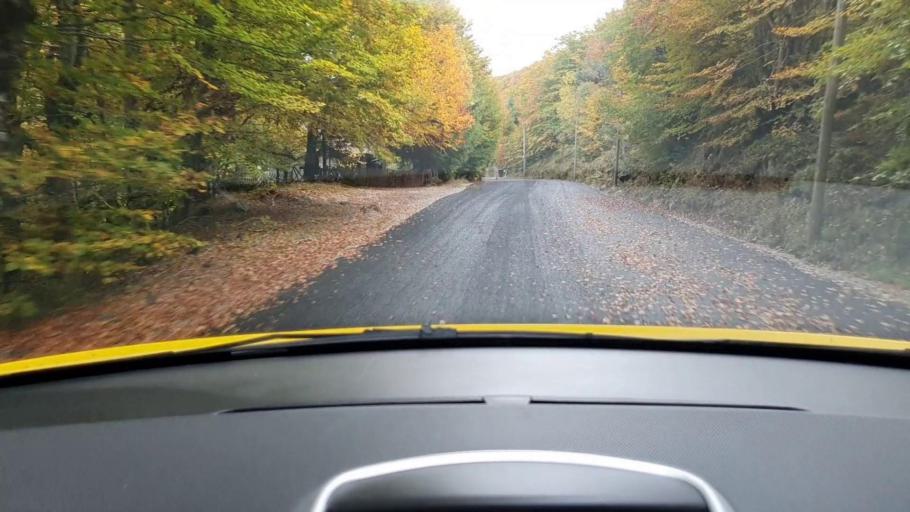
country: FR
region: Languedoc-Roussillon
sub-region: Departement du Gard
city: Valleraugue
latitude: 44.0819
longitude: 3.5389
